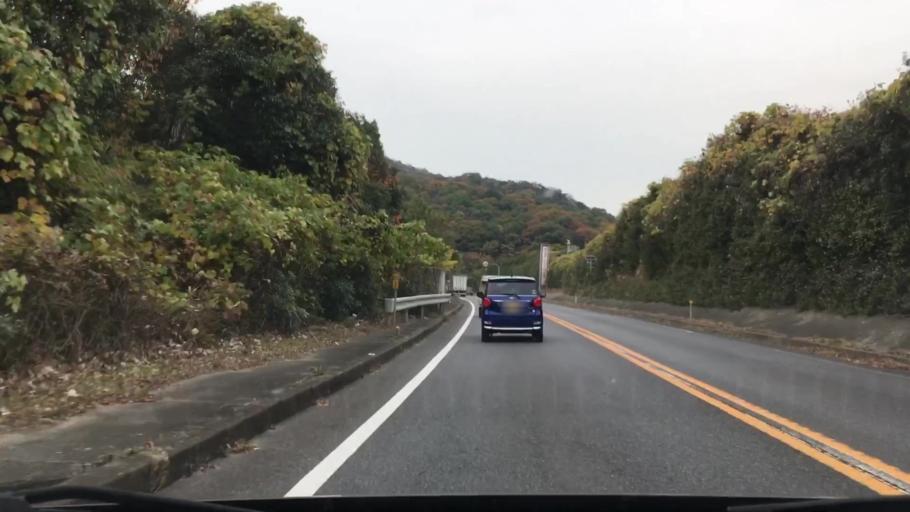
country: JP
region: Yamaguchi
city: Hofu
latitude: 34.0695
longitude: 131.5996
